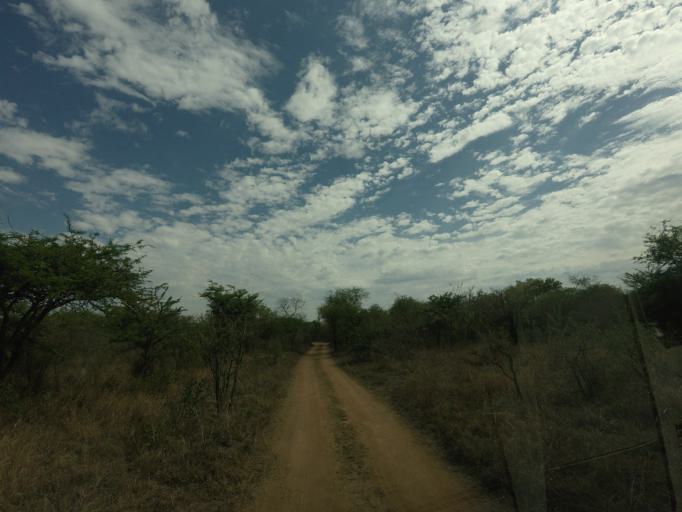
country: ZA
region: Limpopo
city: Thulamahashi
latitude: -24.5235
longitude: 31.1154
